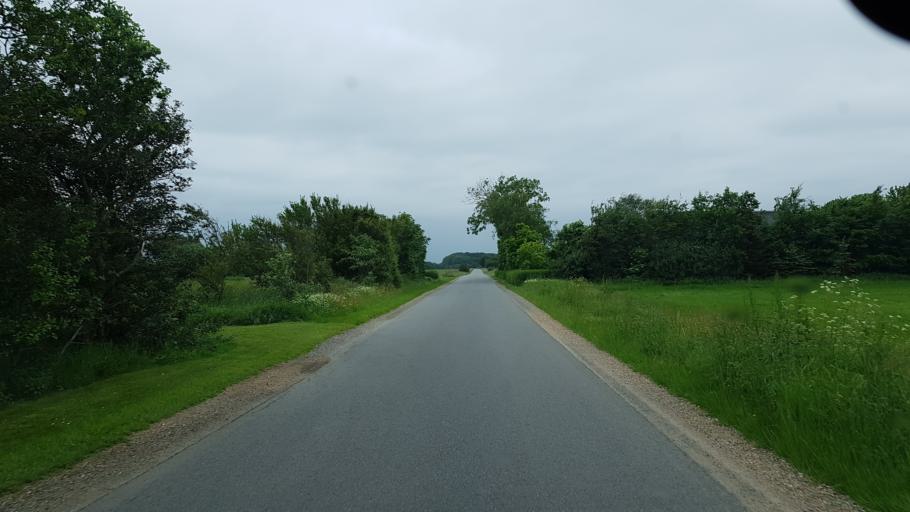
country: DK
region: South Denmark
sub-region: Varde Kommune
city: Olgod
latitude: 55.6754
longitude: 8.7412
